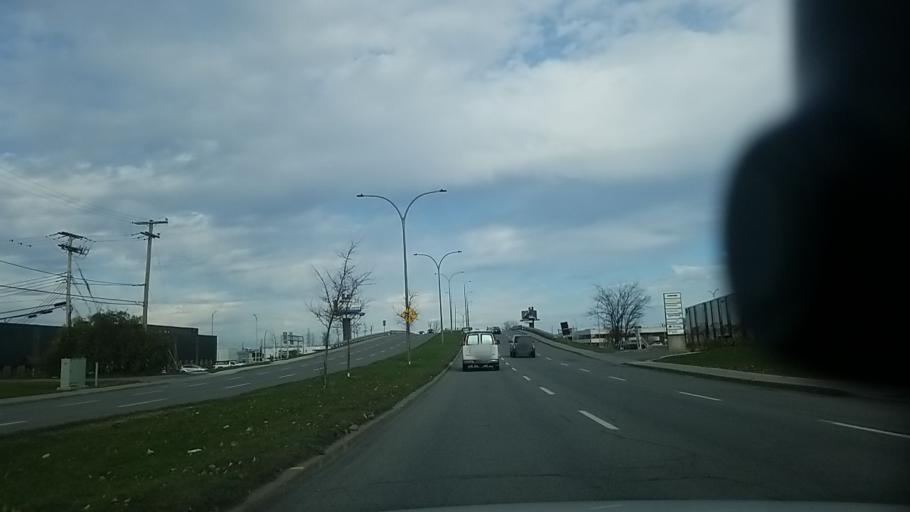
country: CA
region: Quebec
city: Dorval
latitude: 45.4971
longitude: -73.7518
